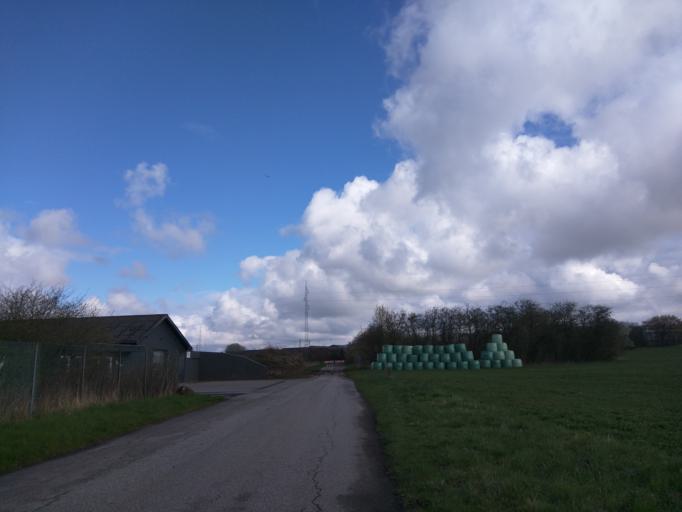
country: DK
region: South Denmark
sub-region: Fredericia Kommune
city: Snoghoj
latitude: 55.5401
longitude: 9.6921
